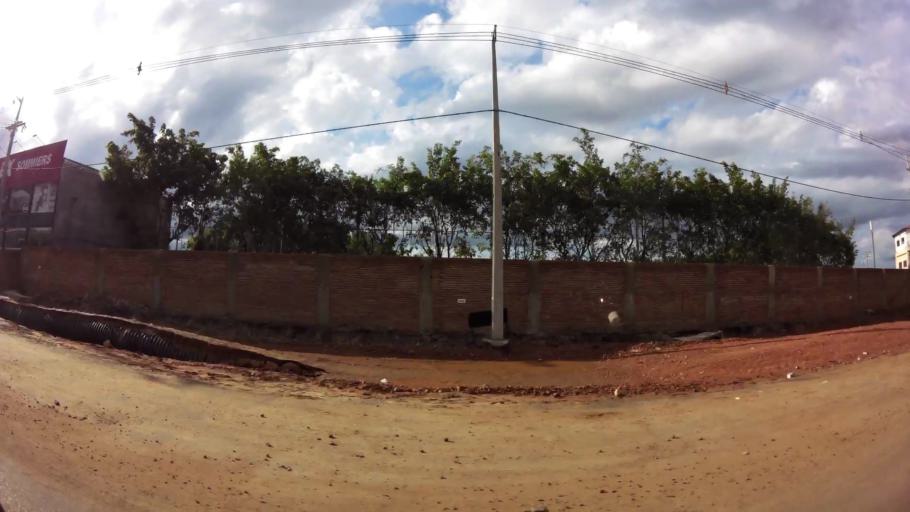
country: PY
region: Central
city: Fernando de la Mora
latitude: -25.2756
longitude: -57.5464
